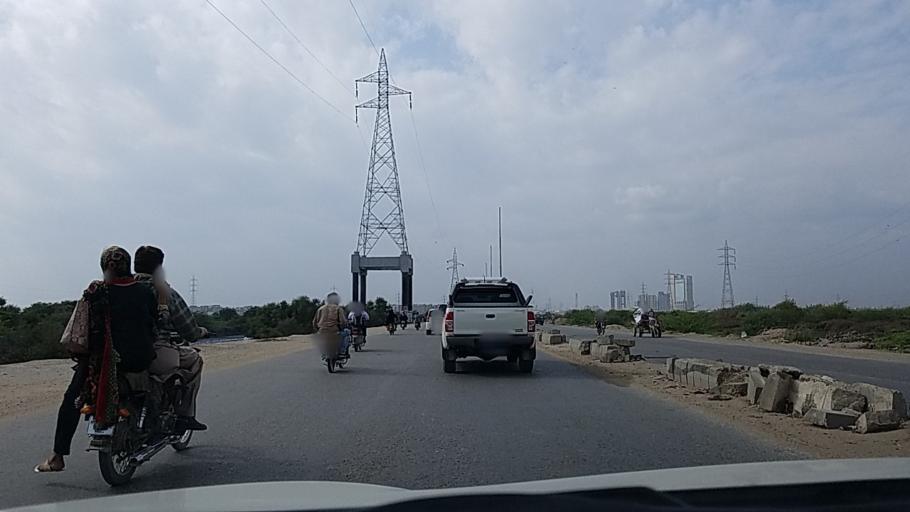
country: PK
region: Sindh
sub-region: Karachi District
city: Karachi
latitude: 24.8219
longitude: 67.0979
